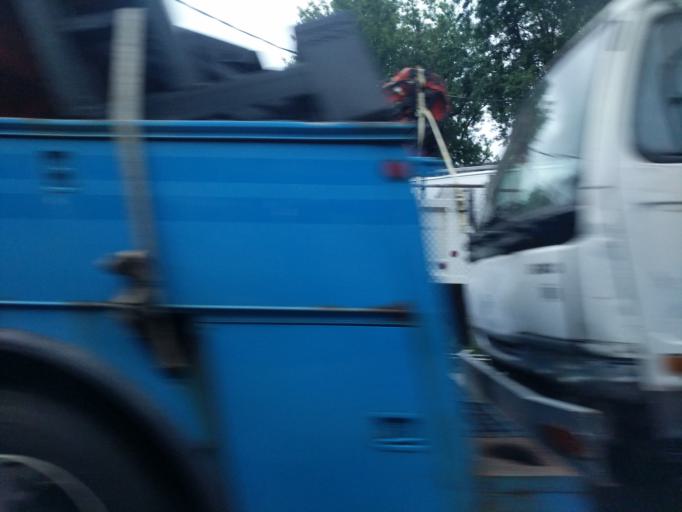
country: US
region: New York
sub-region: Queens County
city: Jamaica
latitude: 40.6821
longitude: -73.7713
